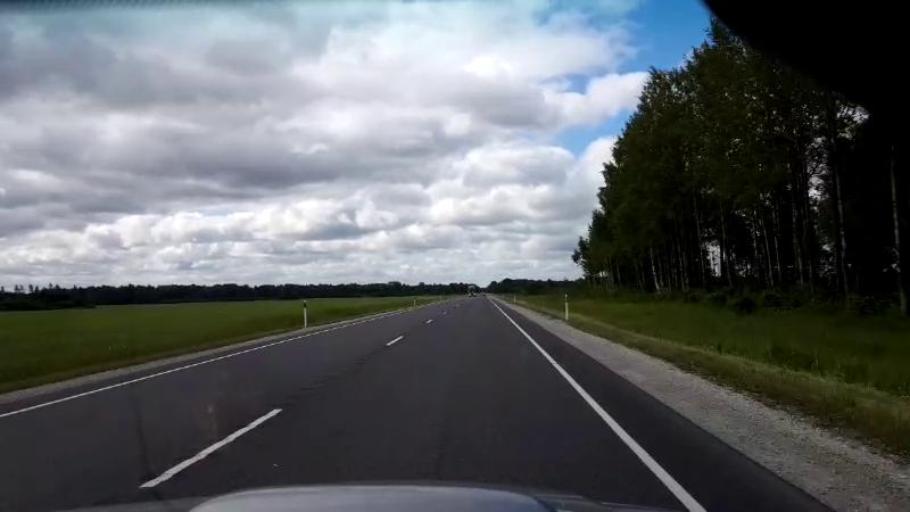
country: EE
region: Raplamaa
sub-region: Maerjamaa vald
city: Marjamaa
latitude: 58.8498
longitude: 24.4296
